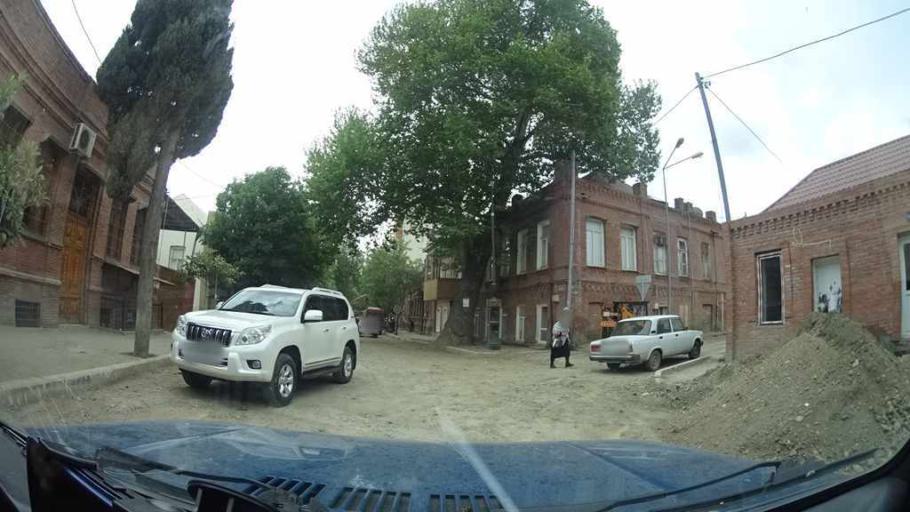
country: AZ
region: Ganja City
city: Ganja
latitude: 40.6776
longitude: 46.3606
